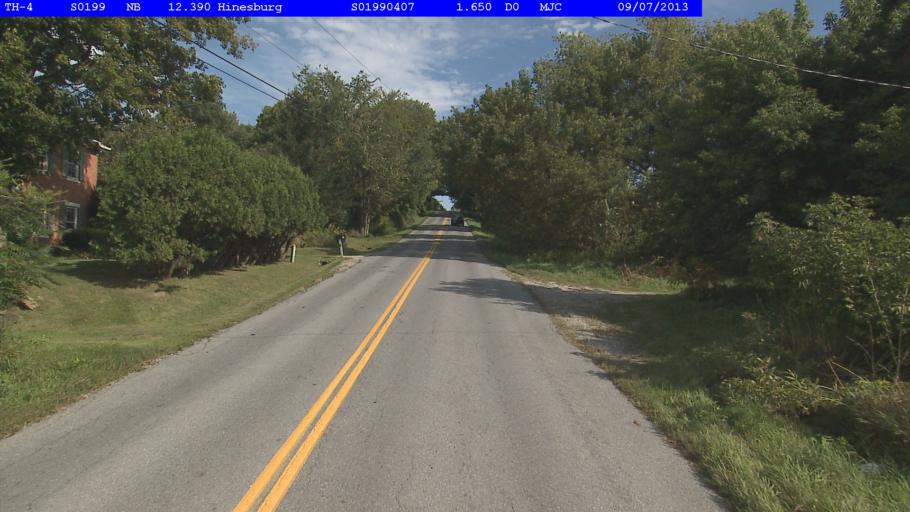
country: US
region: Vermont
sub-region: Chittenden County
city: Hinesburg
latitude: 44.3017
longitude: -73.1094
